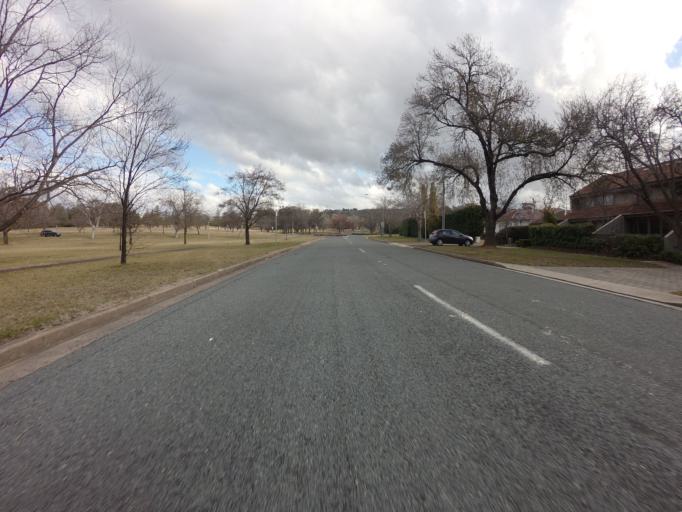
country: AU
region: Australian Capital Territory
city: Forrest
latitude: -35.3178
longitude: 149.1247
